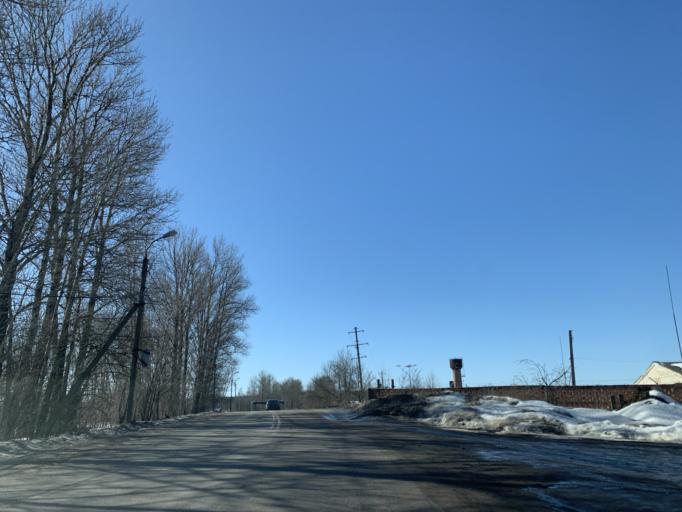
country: RU
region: Jaroslavl
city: Konstantinovskiy
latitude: 57.8378
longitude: 39.5653
